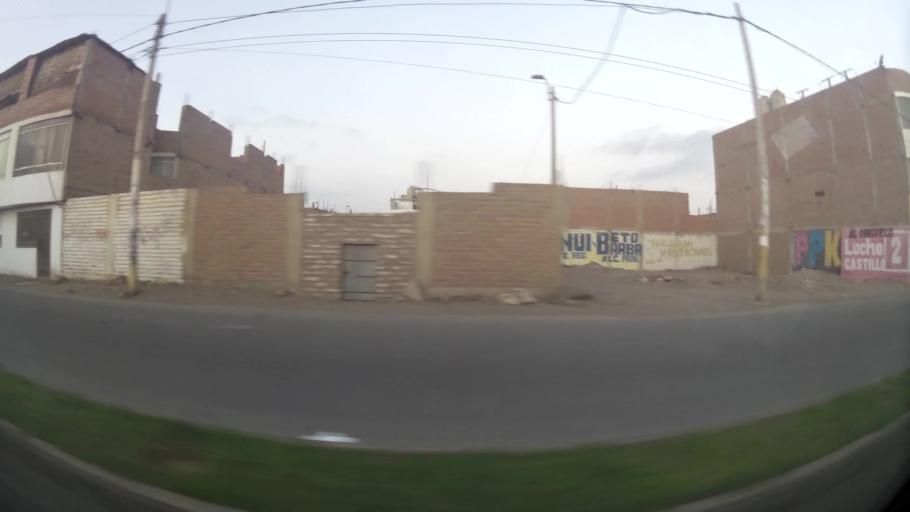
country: PE
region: Lima
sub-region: Huaura
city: Huacho
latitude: -11.1208
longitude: -77.6058
